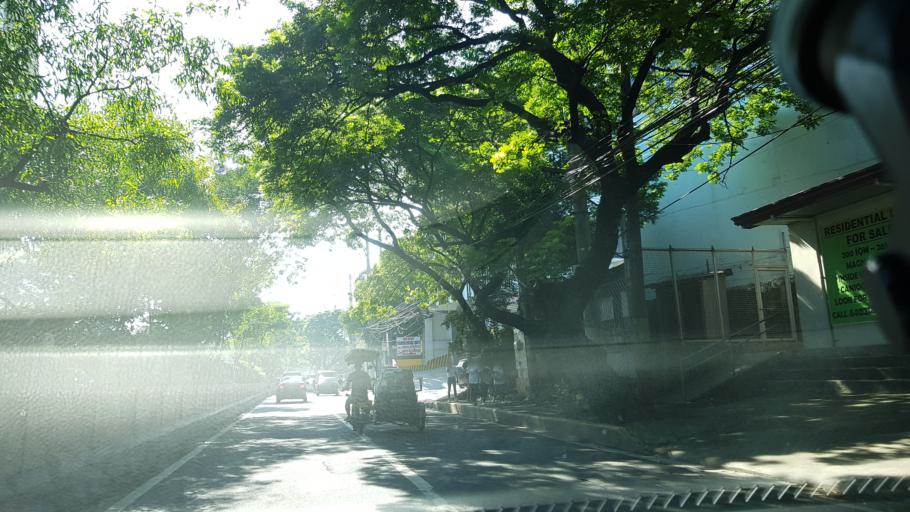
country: PH
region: Metro Manila
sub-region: Pasig
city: Pasig City
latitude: 14.5692
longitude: 121.0842
